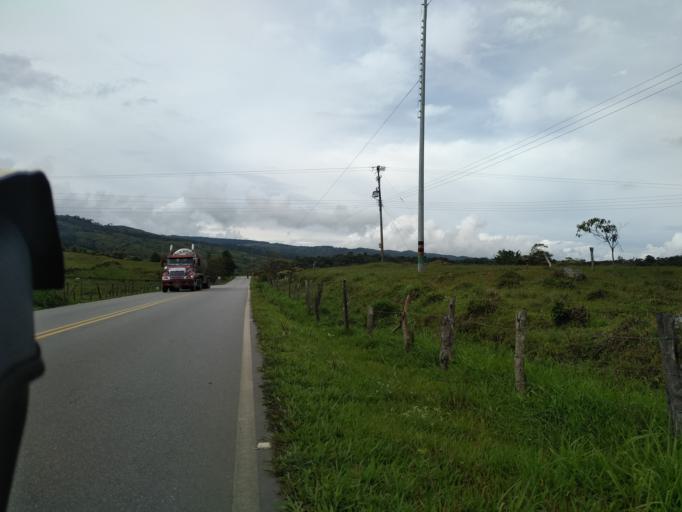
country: CO
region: Santander
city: Suaita
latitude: 6.1147
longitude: -73.3673
